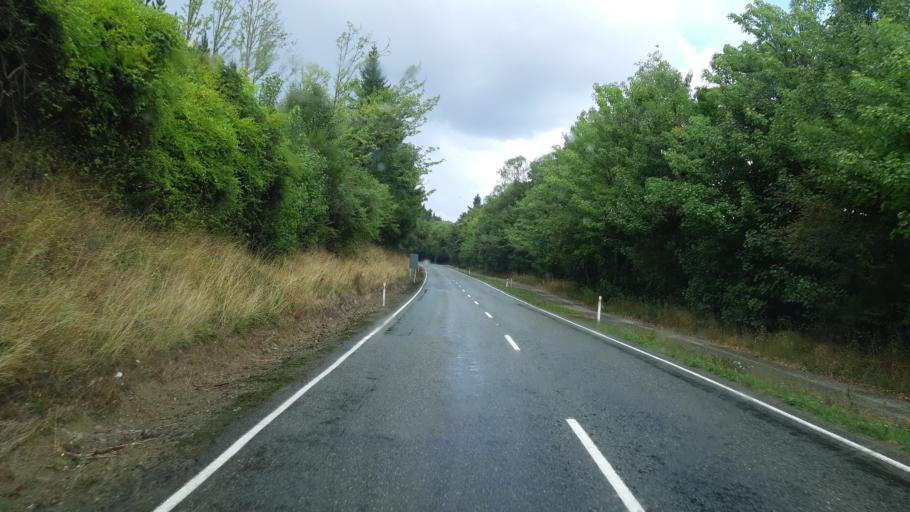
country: NZ
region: Tasman
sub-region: Tasman District
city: Wakefield
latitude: -41.4679
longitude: 172.8409
